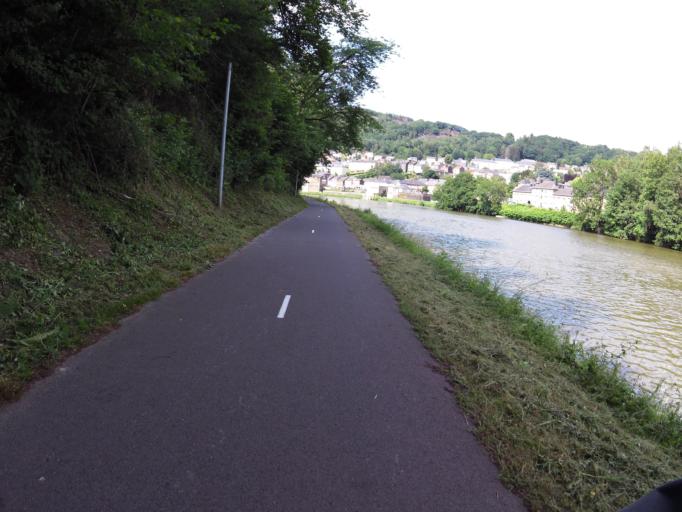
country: FR
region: Champagne-Ardenne
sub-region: Departement des Ardennes
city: Montherme
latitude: 49.8826
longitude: 4.7370
